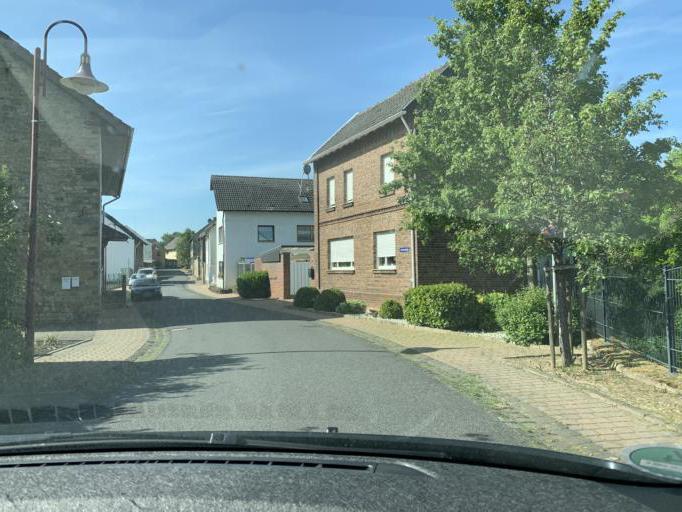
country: DE
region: North Rhine-Westphalia
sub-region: Regierungsbezirk Koln
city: Vettweiss
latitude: 50.6719
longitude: 6.5637
